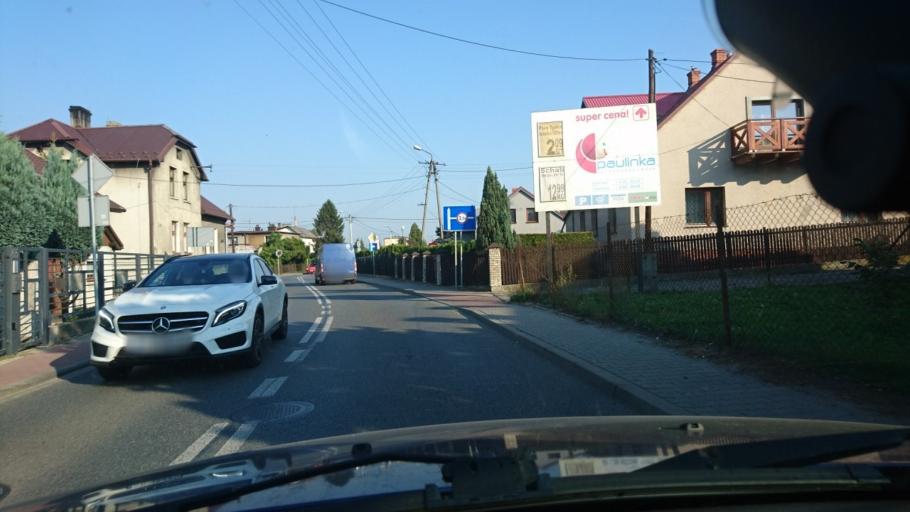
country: PL
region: Silesian Voivodeship
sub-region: Bielsko-Biala
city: Bielsko-Biala
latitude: 49.8512
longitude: 19.0505
